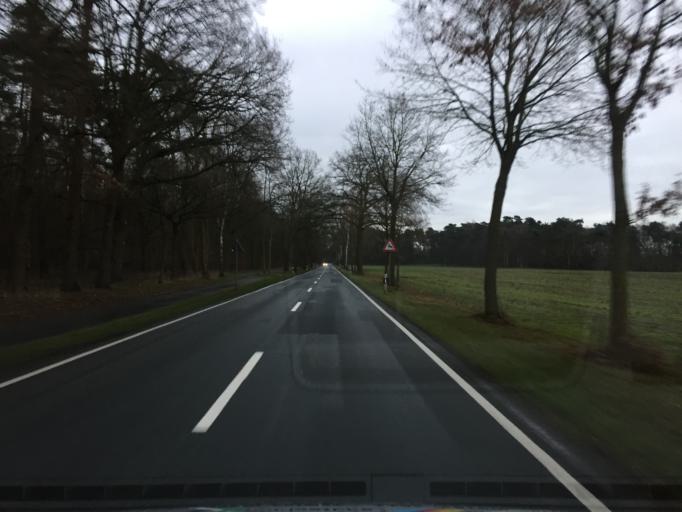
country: DE
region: Lower Saxony
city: Steyerberg
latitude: 52.5830
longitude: 8.9952
